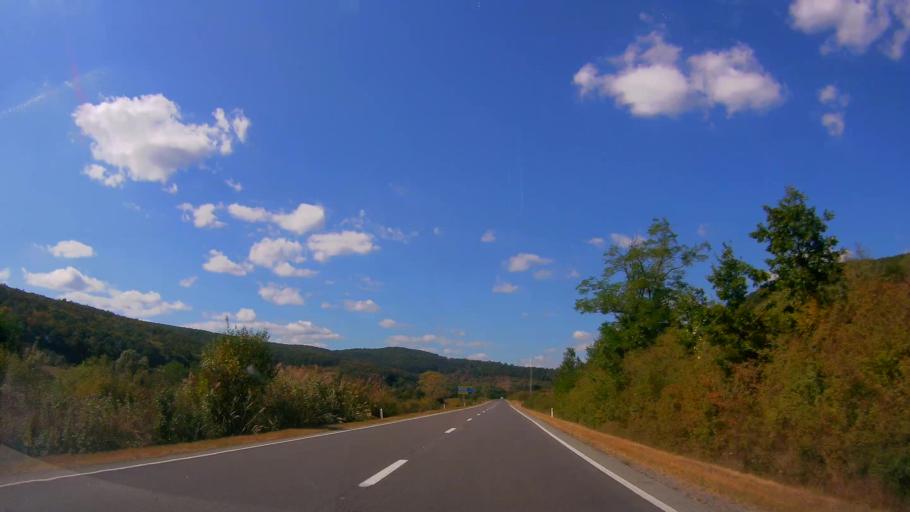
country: RO
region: Salaj
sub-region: Comuna Zimbor
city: Zimbor
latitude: 46.9710
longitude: 23.2645
